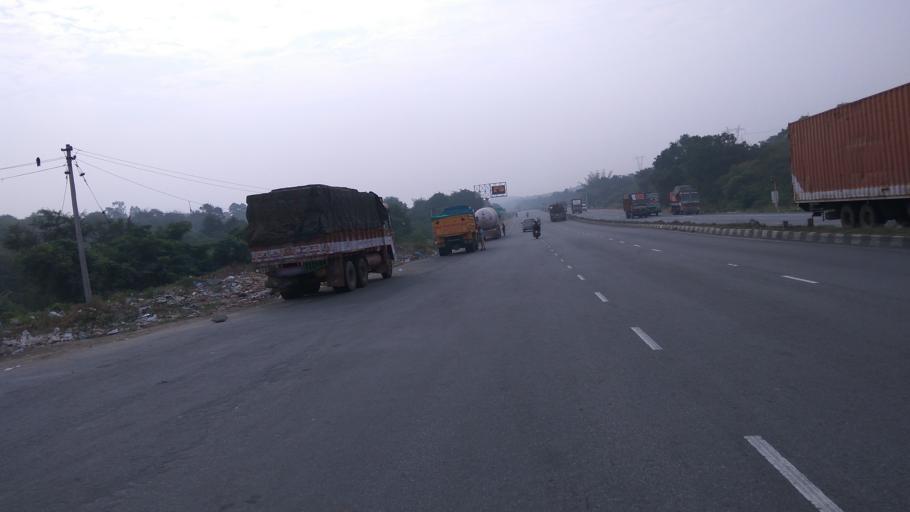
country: IN
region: Tamil Nadu
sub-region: Krishnagiri
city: Hosur
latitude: 12.7081
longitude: 77.9009
